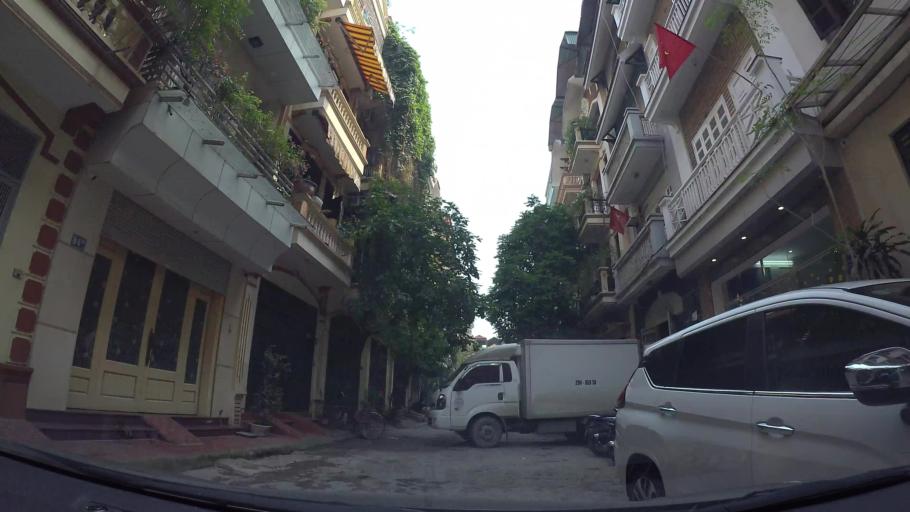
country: VN
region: Ha Noi
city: Van Dien
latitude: 20.9746
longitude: 105.8348
